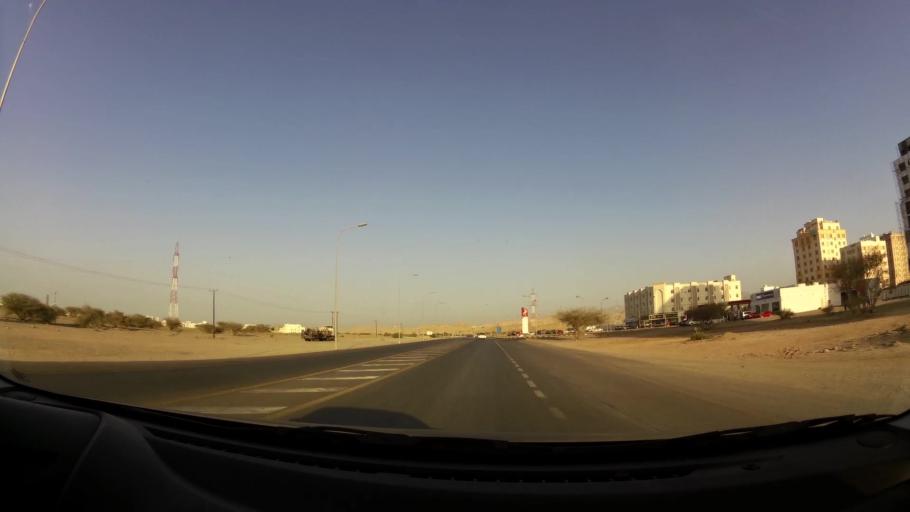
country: OM
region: Muhafazat Masqat
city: As Sib al Jadidah
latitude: 23.5759
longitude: 58.1827
